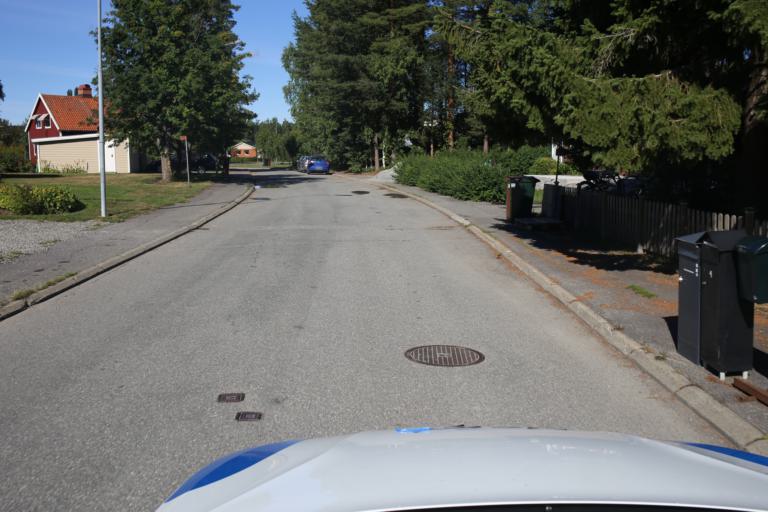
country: SE
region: Vaesterbotten
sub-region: Skelleftea Kommun
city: Viken
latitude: 64.7463
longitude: 20.7695
